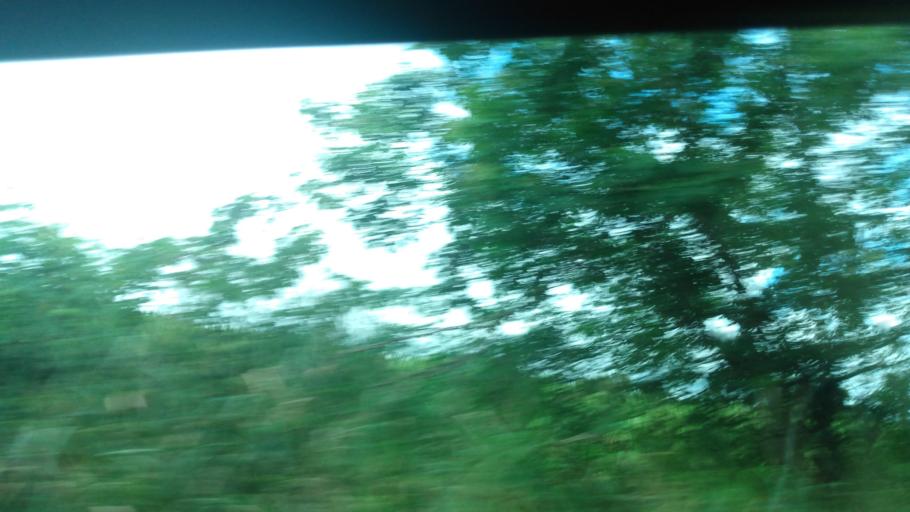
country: BR
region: Pernambuco
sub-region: Quipapa
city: Quipapa
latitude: -8.7832
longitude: -35.9500
